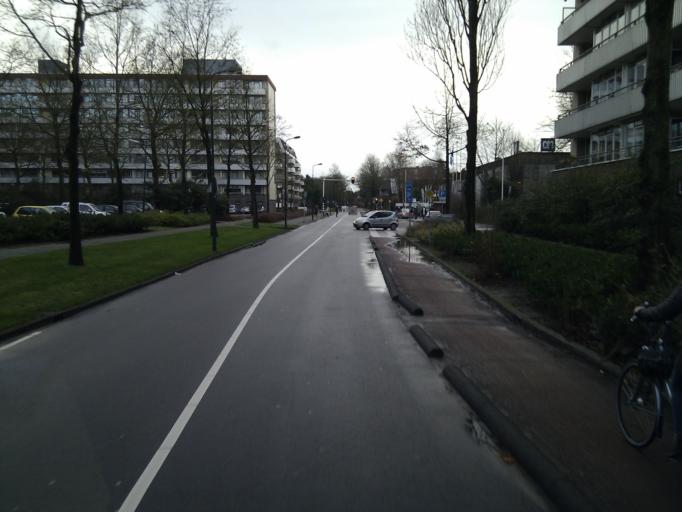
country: NL
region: Utrecht
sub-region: Gemeente De Bilt
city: De Bilt
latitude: 52.1285
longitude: 5.2113
